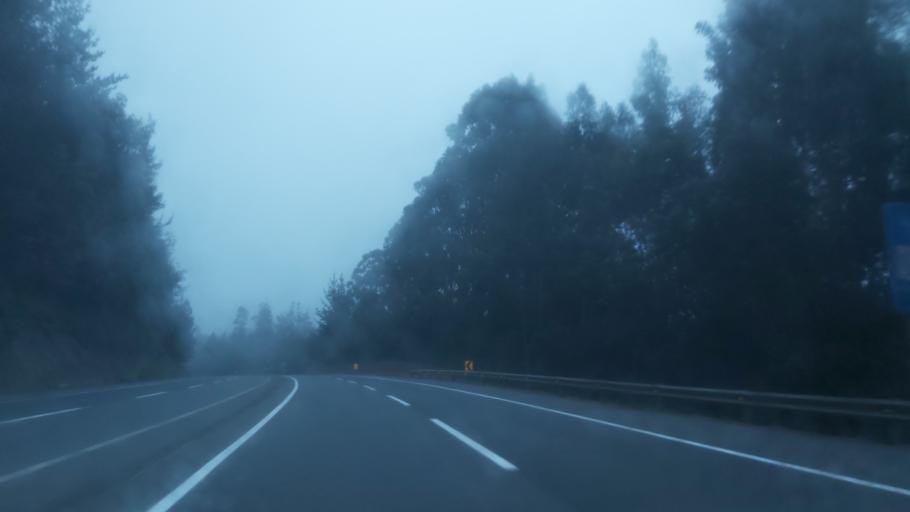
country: CL
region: Biobio
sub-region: Provincia de Concepcion
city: Penco
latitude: -36.7422
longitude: -72.9094
